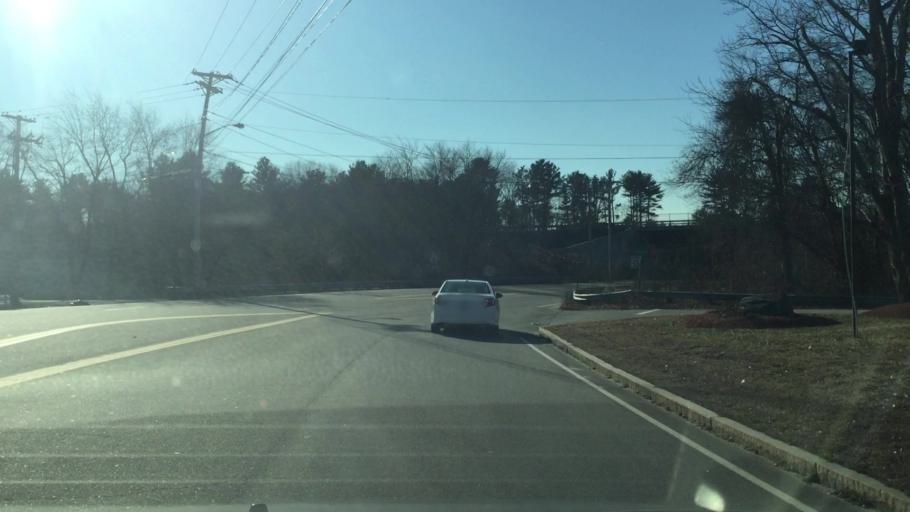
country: US
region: New Hampshire
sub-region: Rockingham County
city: Salem
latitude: 42.7659
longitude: -71.2349
